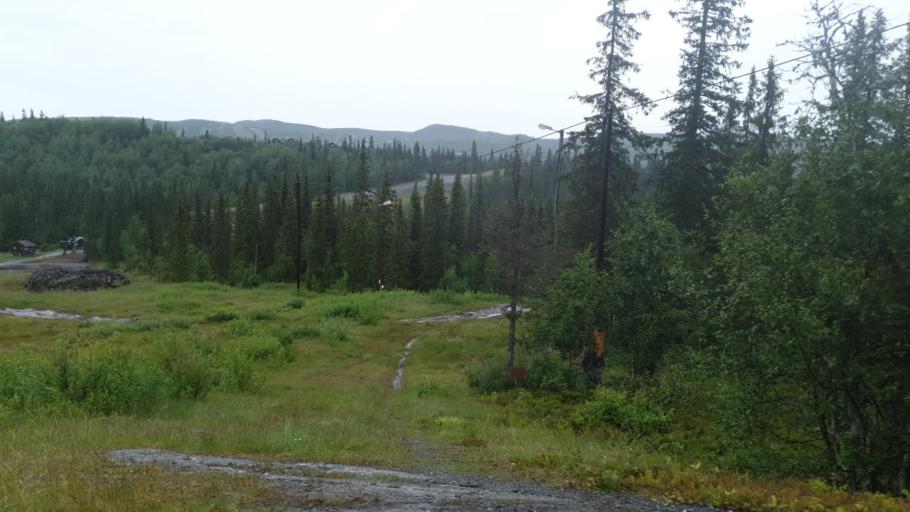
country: NO
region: Oppland
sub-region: Vestre Slidre
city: Slidre
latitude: 61.2313
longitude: 8.9118
